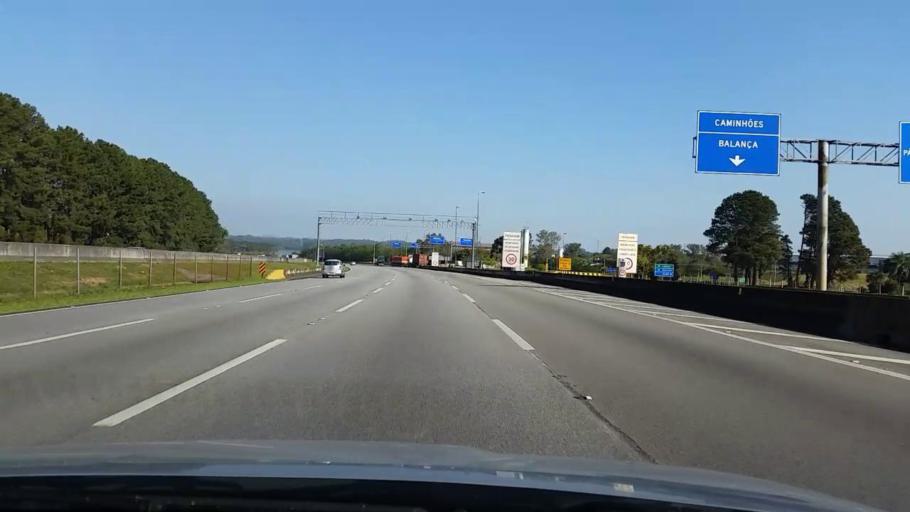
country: BR
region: Sao Paulo
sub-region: Sao Bernardo Do Campo
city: Sao Bernardo do Campo
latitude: -23.7816
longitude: -46.5978
